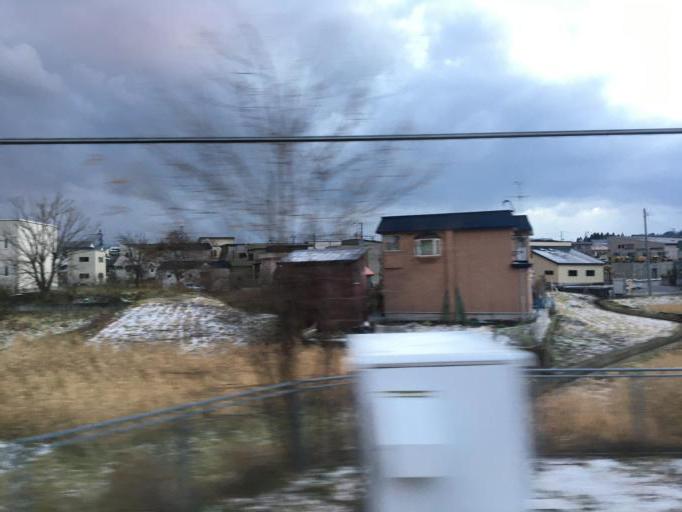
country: JP
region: Aomori
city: Aomori Shi
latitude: 40.8277
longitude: 140.6899
